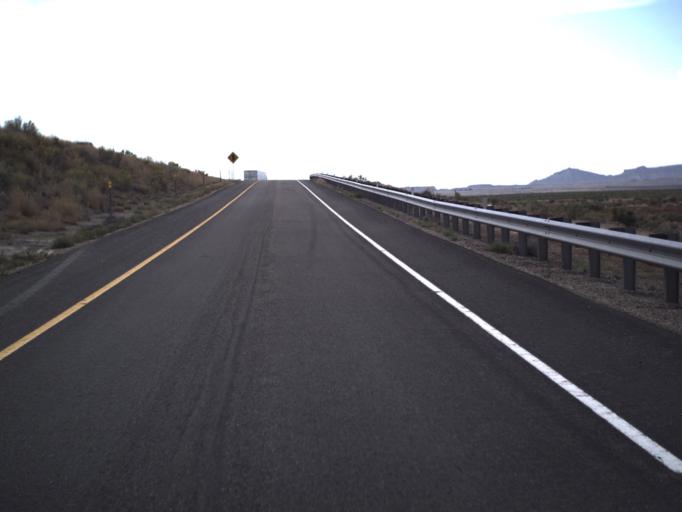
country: US
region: Utah
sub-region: Grand County
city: Moab
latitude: 38.9620
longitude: -109.7254
